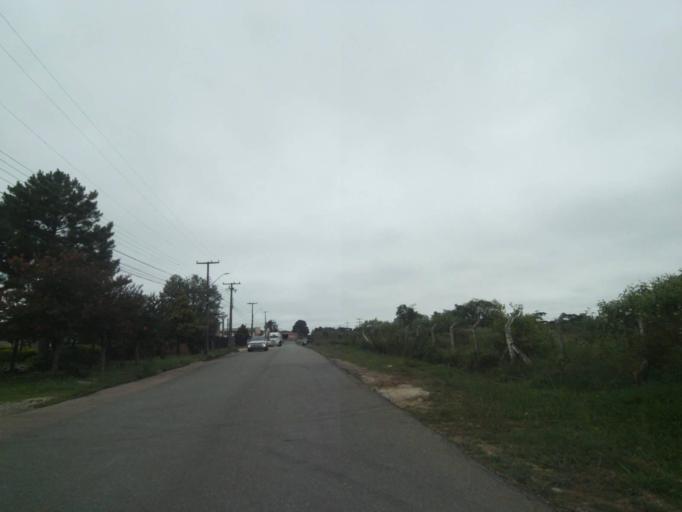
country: BR
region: Parana
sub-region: Araucaria
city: Araucaria
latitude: -25.5448
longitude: -49.3333
